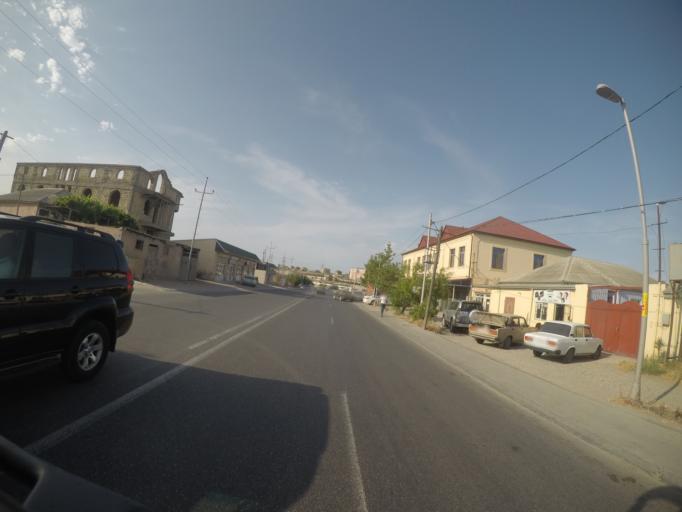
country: AZ
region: Baki
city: Binagadi
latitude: 40.4782
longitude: 49.8339
